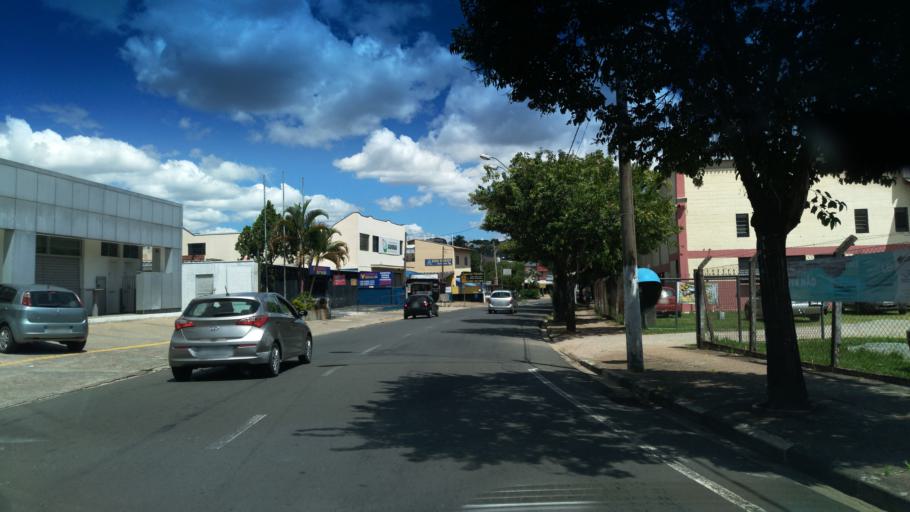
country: BR
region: Sao Paulo
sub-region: Valinhos
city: Valinhos
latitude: -22.9609
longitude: -46.9876
